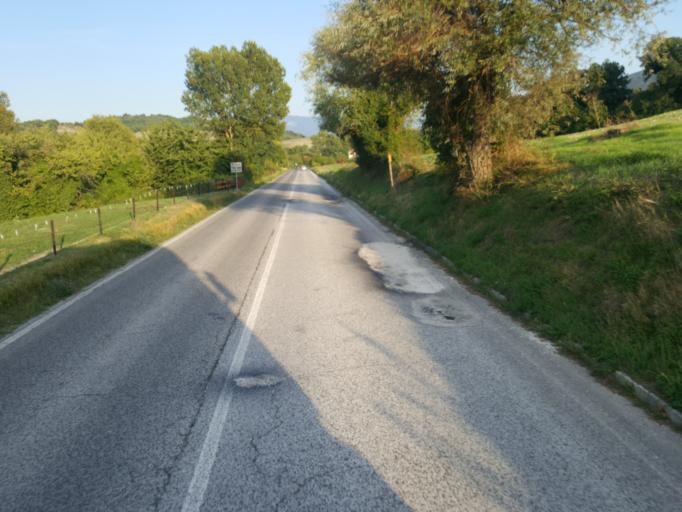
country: IT
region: The Marches
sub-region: Provincia di Ancona
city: Fabriano
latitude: 43.3505
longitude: 12.8308
